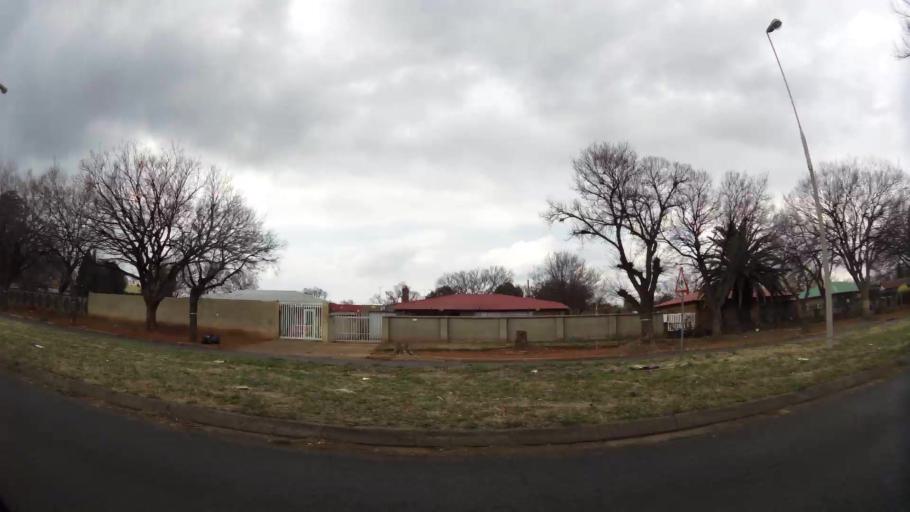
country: ZA
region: Gauteng
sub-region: Sedibeng District Municipality
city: Vanderbijlpark
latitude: -26.7006
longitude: 27.8230
